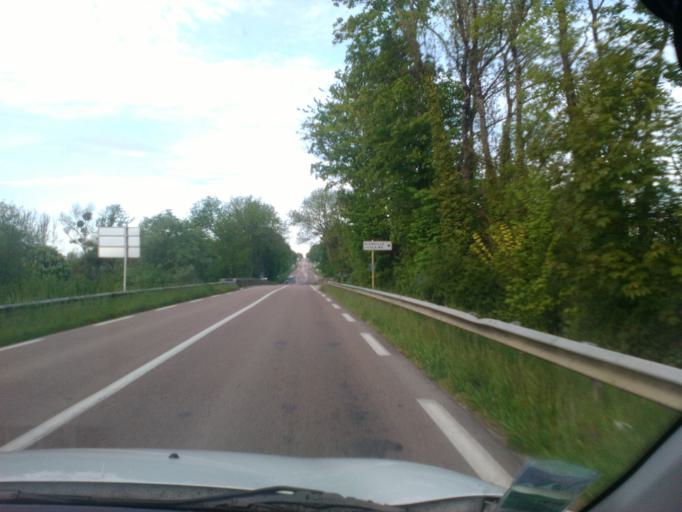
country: FR
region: Champagne-Ardenne
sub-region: Departement de l'Aube
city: Bar-sur-Aube
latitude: 48.2723
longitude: 4.6200
